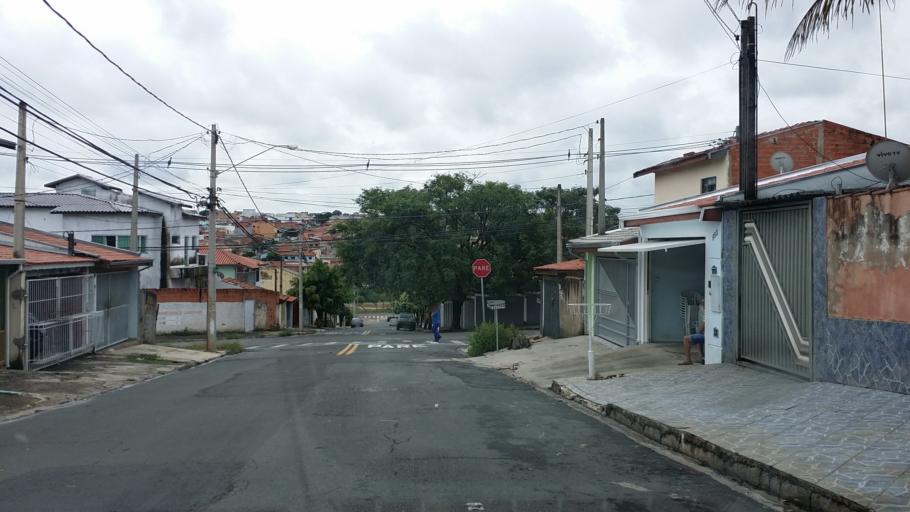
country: BR
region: Sao Paulo
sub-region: Indaiatuba
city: Indaiatuba
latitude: -23.1264
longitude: -47.2307
